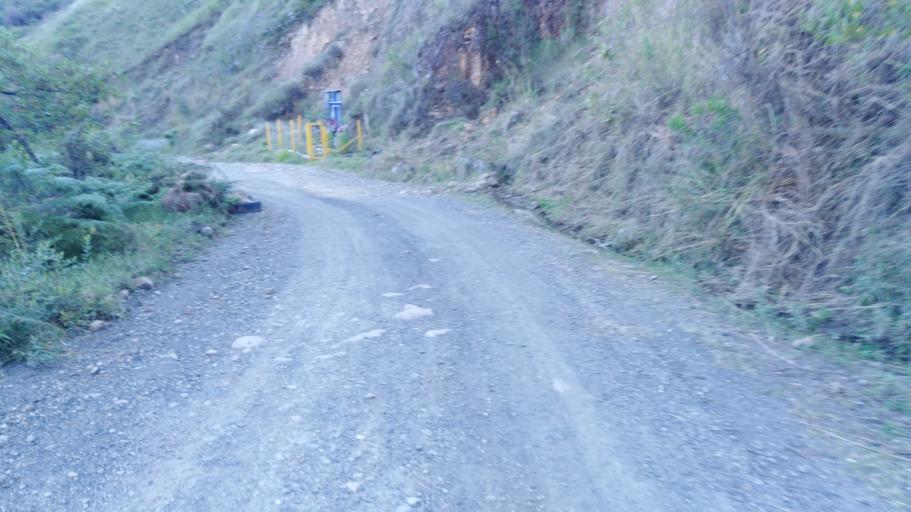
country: CO
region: Boyaca
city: San Mateo
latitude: 6.4012
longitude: -72.5627
